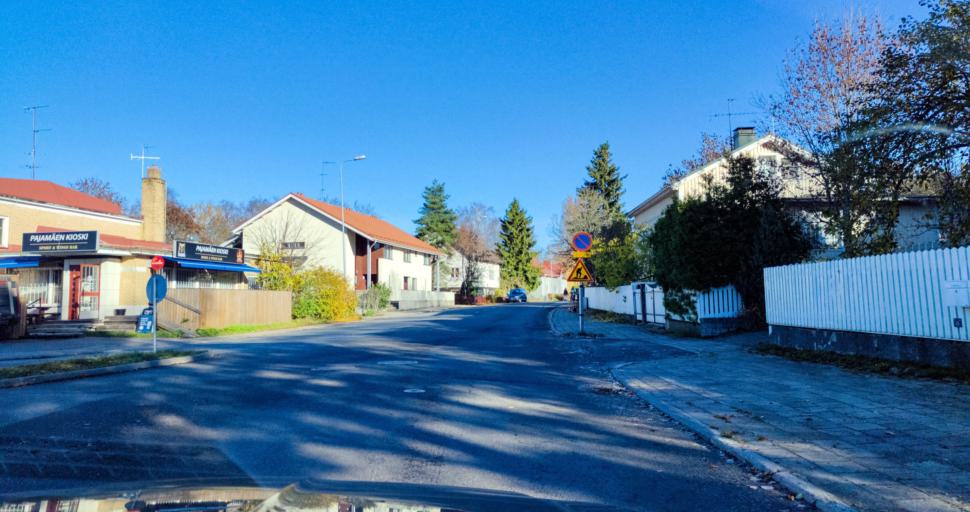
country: FI
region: Varsinais-Suomi
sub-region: Turku
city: Turku
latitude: 60.4349
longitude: 22.2598
